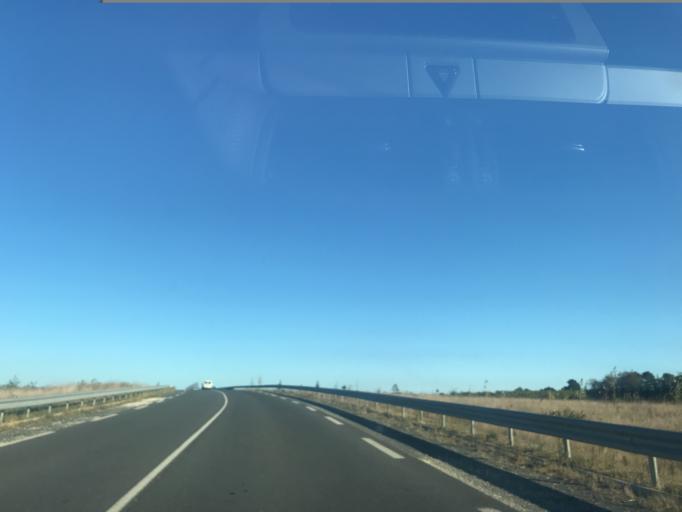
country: FR
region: Poitou-Charentes
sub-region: Departement de la Charente-Maritime
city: Montguyon
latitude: 45.2103
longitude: -0.1709
